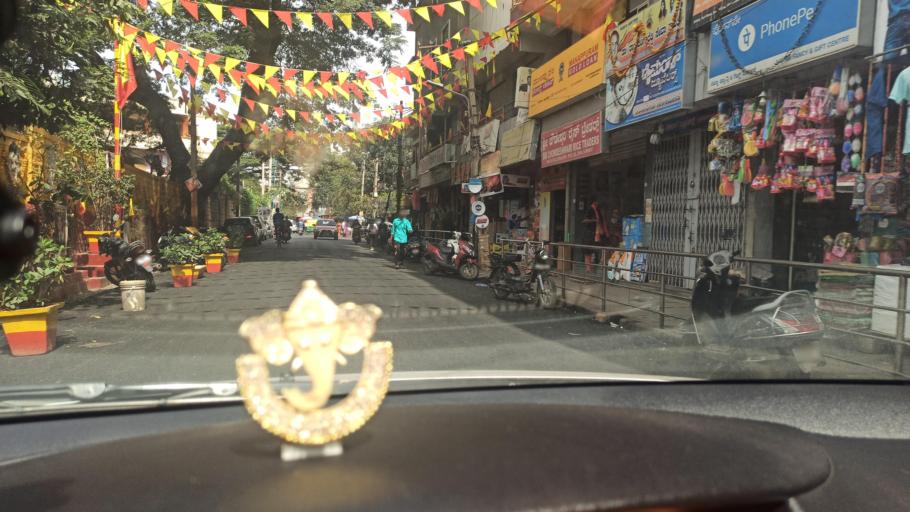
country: IN
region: Karnataka
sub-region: Bangalore Urban
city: Bangalore
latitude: 12.9213
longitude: 77.6333
